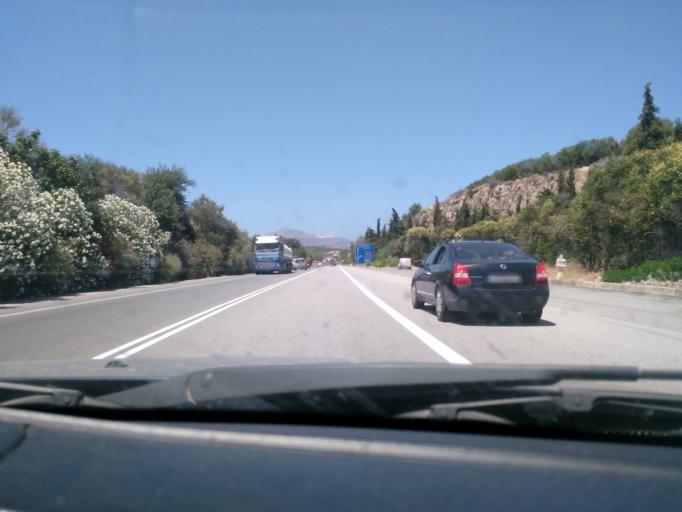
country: GR
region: Crete
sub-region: Nomos Chanias
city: Kalivai
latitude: 35.4335
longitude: 24.1659
